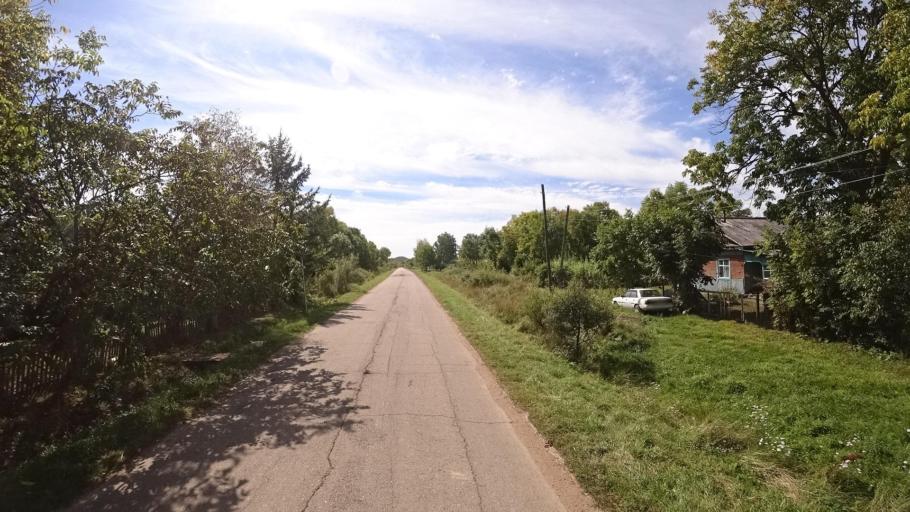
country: RU
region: Primorskiy
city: Kirovskiy
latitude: 44.7563
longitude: 133.6069
